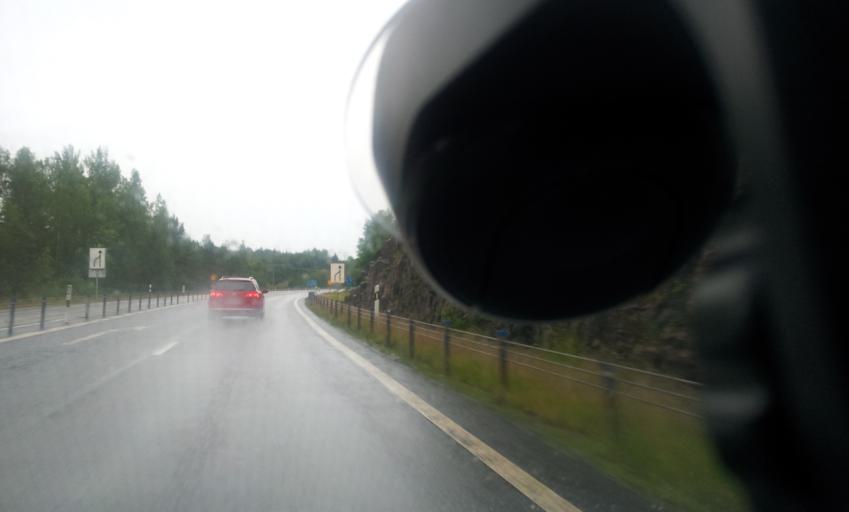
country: SE
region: OEstergoetland
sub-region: Valdemarsviks Kommun
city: Valdemarsvik
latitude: 58.1902
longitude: 16.5372
